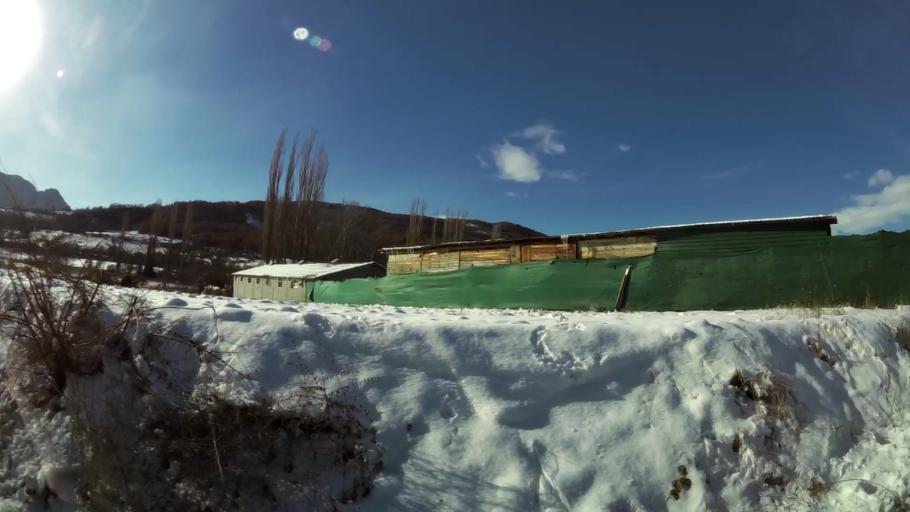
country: MK
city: Ljubin
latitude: 41.9861
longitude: 21.2973
